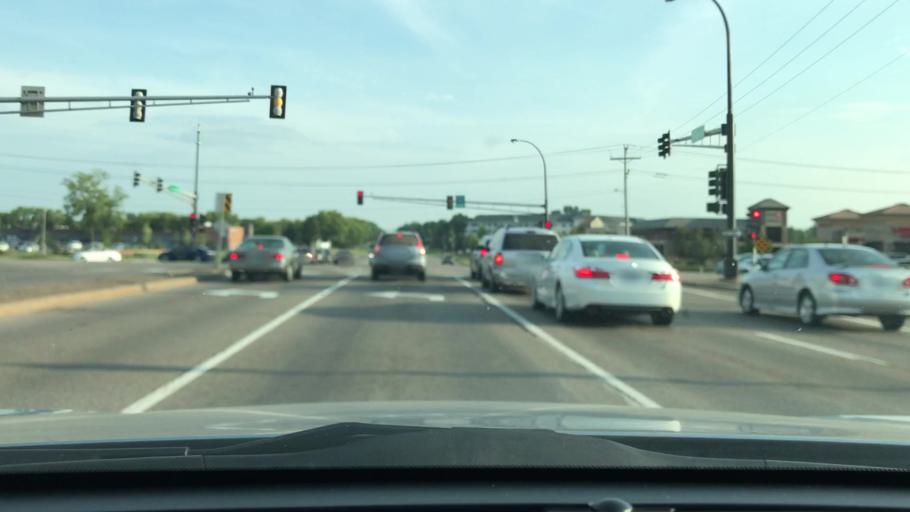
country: US
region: Minnesota
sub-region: Hennepin County
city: Plymouth
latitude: 45.0192
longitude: -93.4818
